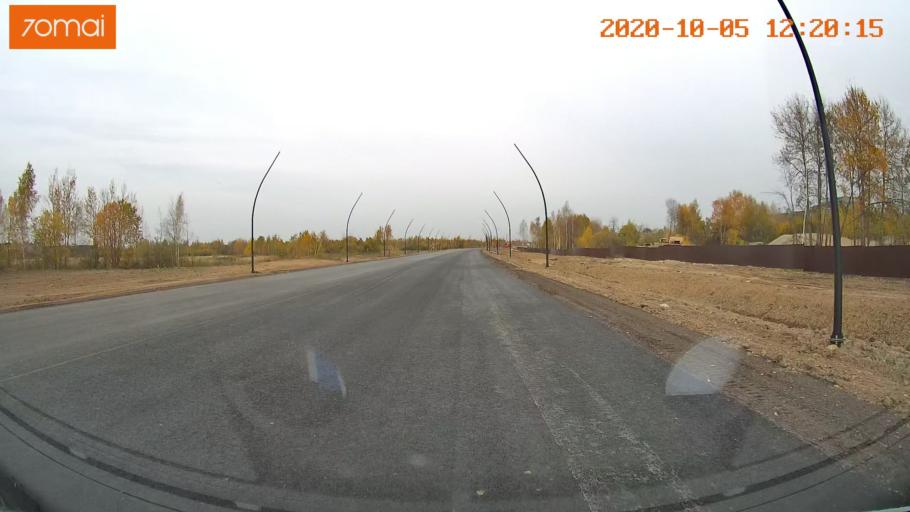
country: RU
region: Ivanovo
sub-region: Gorod Ivanovo
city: Ivanovo
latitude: 56.9614
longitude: 40.9308
